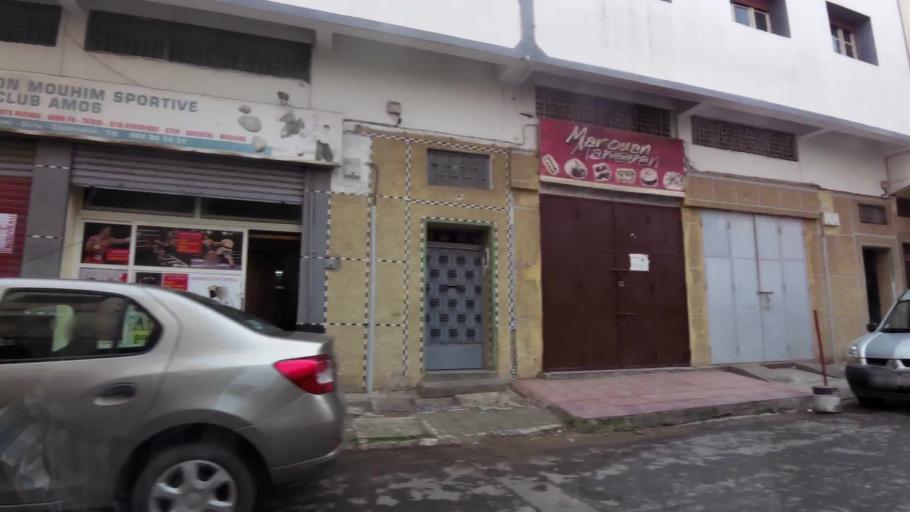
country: MA
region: Grand Casablanca
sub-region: Casablanca
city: Casablanca
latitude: 33.5660
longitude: -7.6729
